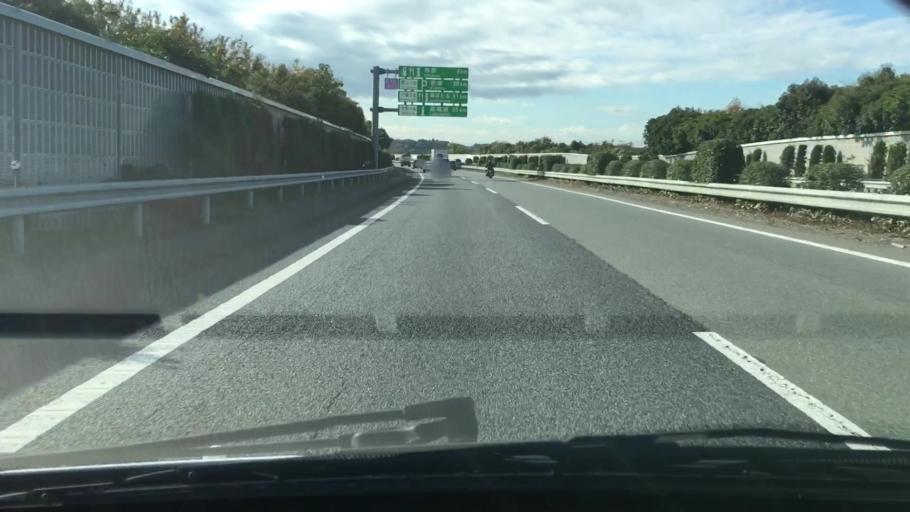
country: JP
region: Chiba
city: Ichihara
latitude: 35.4869
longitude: 140.0837
